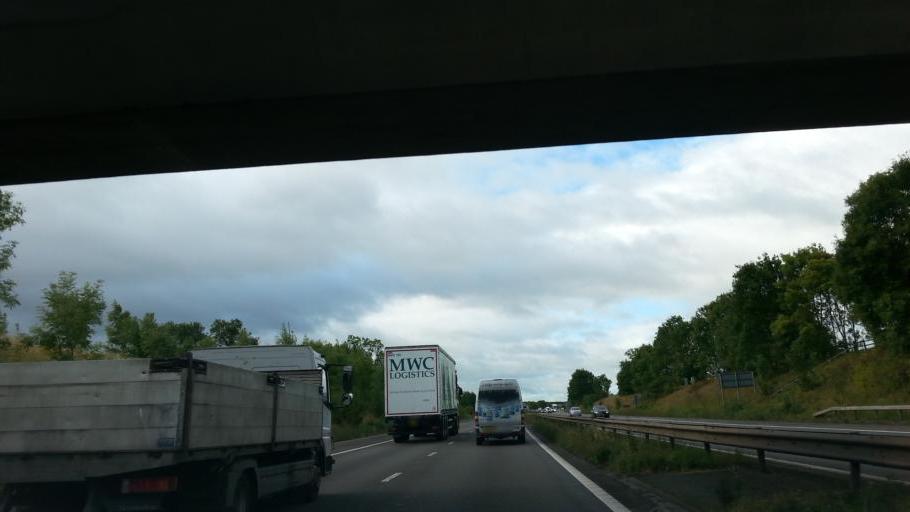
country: GB
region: England
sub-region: Derbyshire
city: Netherseal
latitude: 52.6826
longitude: -1.5515
